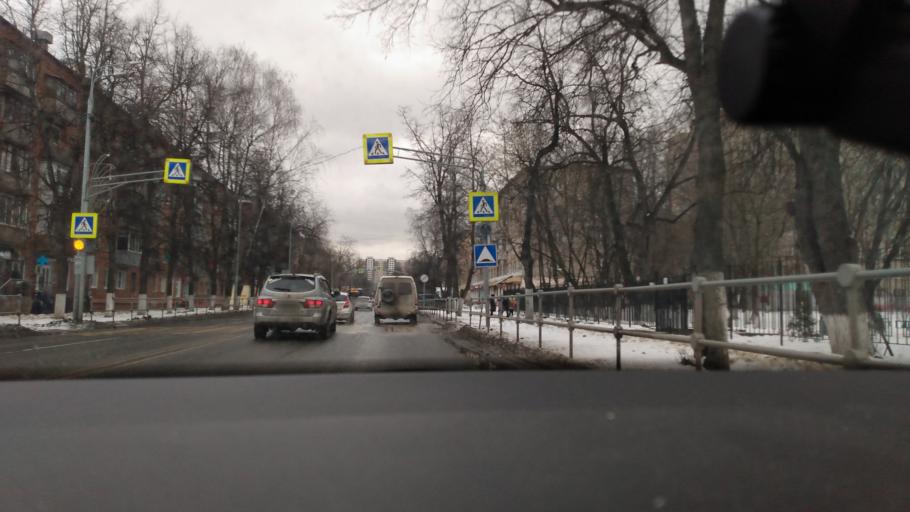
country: RU
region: Moskovskaya
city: Balashikha
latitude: 55.8025
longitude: 37.9347
